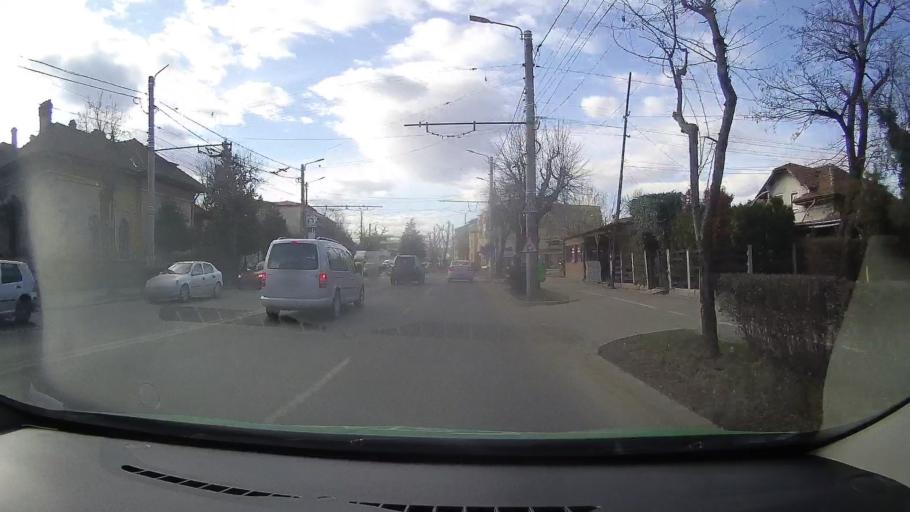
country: RO
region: Dambovita
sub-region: Comuna Lucieni
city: Lucieni
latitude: 44.8616
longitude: 25.4142
